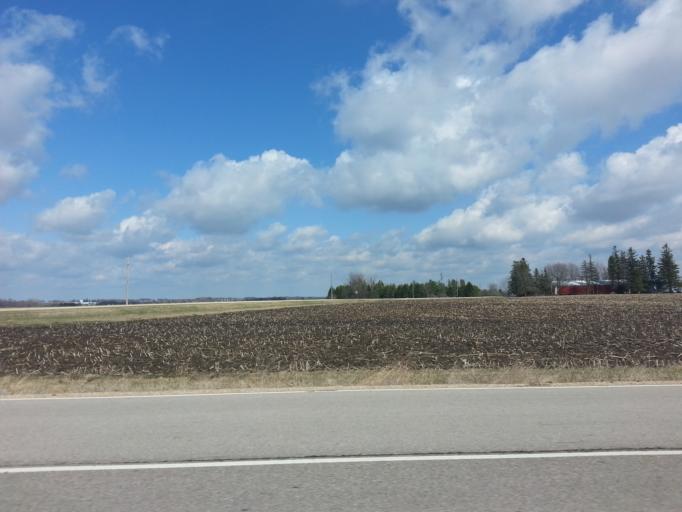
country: US
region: Minnesota
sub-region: Goodhue County
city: Kenyon
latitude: 44.1966
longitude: -92.9240
